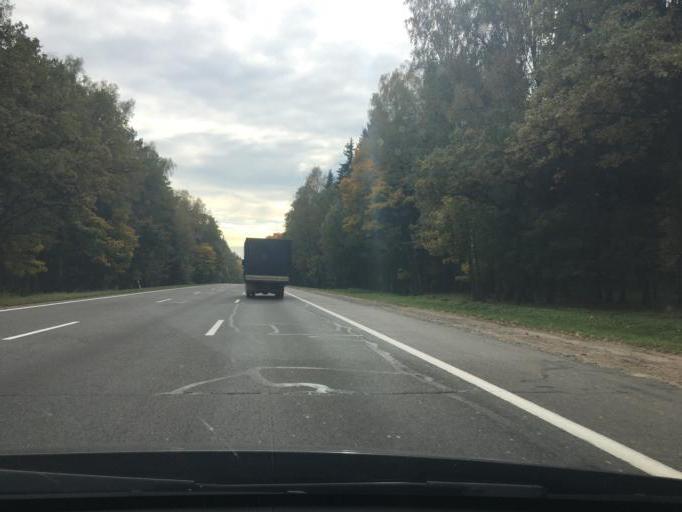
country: BY
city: Fanipol
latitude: 53.7885
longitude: 27.3650
